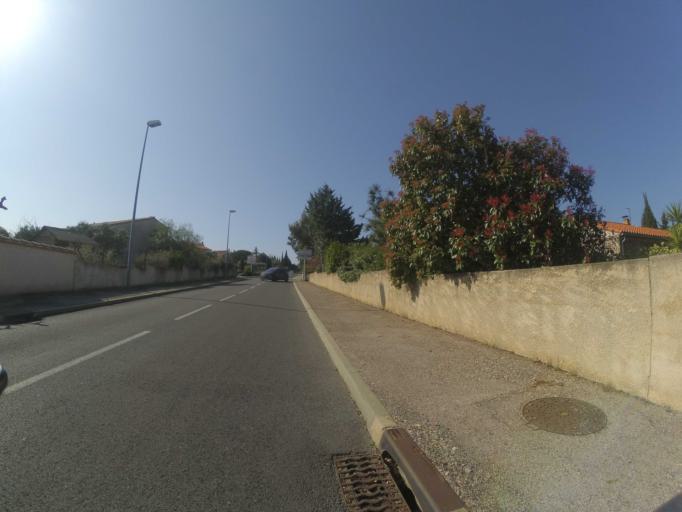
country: FR
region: Languedoc-Roussillon
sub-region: Departement des Pyrenees-Orientales
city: Thuir
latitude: 42.6212
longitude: 2.7510
